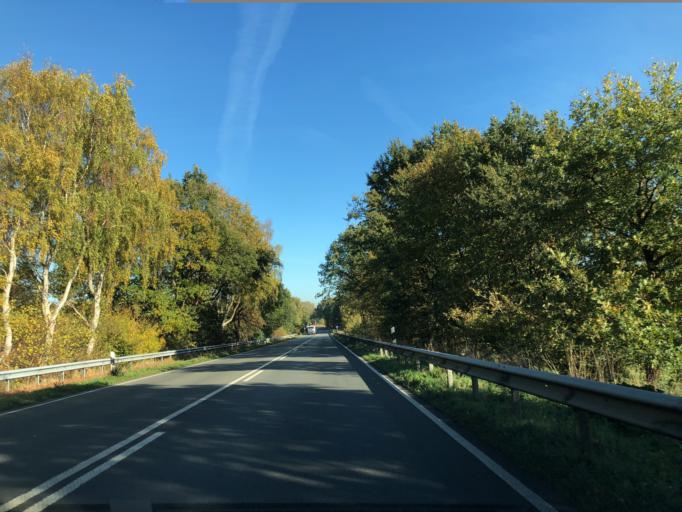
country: DE
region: Lower Saxony
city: Lehe
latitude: 53.0455
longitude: 7.3372
